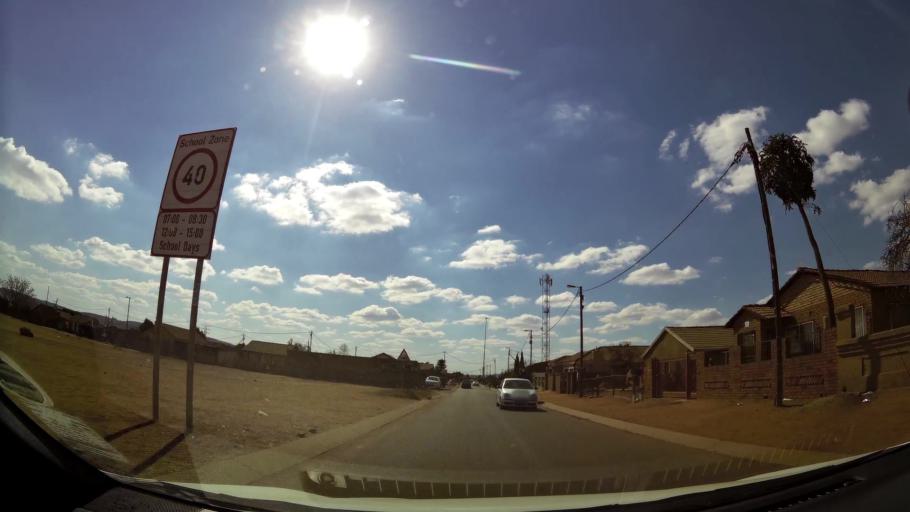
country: ZA
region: Gauteng
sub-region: City of Tshwane Metropolitan Municipality
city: Cullinan
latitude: -25.7228
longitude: 28.4034
